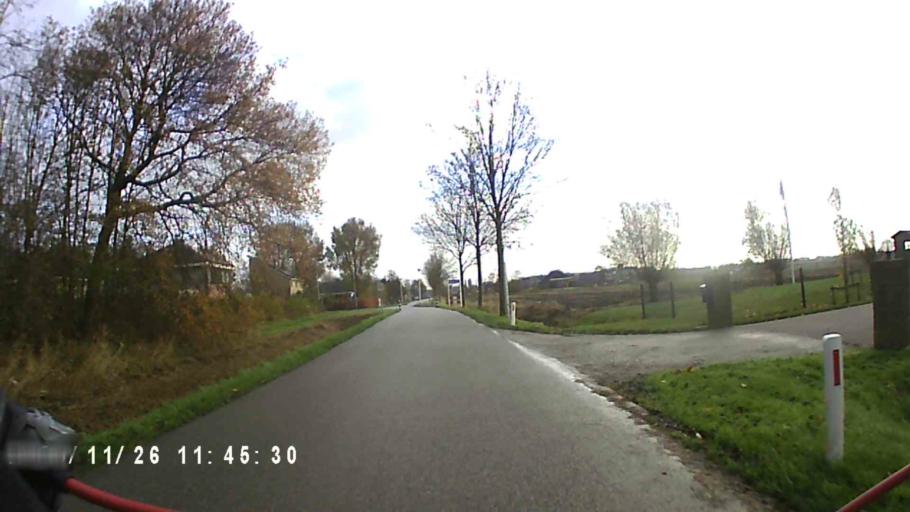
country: NL
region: Groningen
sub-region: Gemeente Bedum
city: Bedum
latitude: 53.3012
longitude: 6.5843
